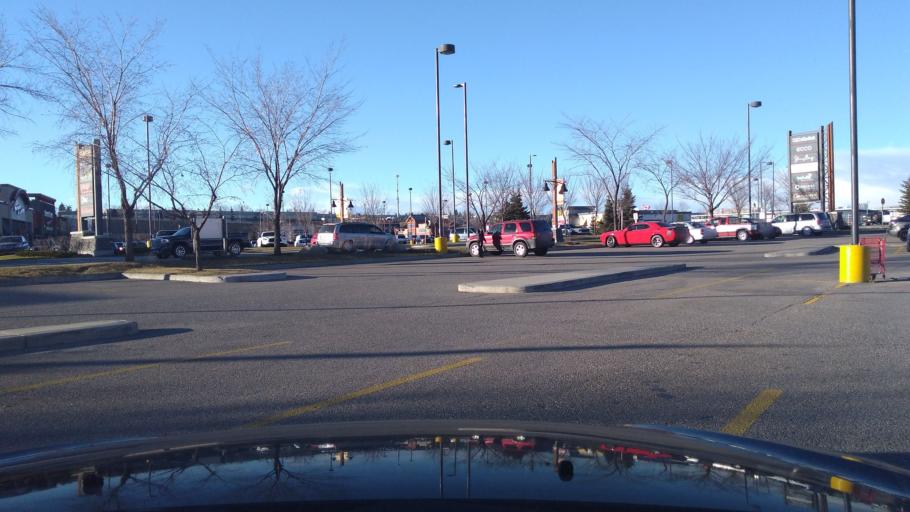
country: CA
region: Alberta
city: Calgary
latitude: 50.9822
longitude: -114.0398
